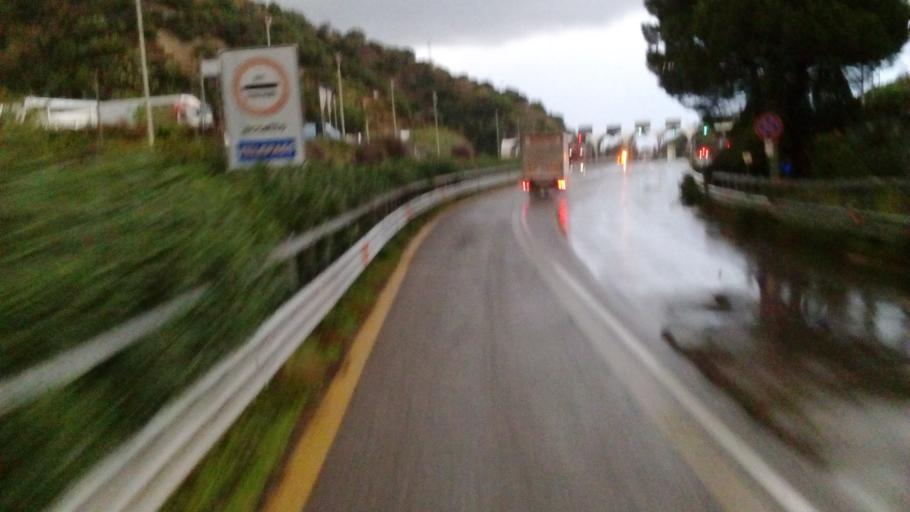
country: IT
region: Sicily
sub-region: Messina
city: Larderia
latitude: 38.1231
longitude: 15.5158
